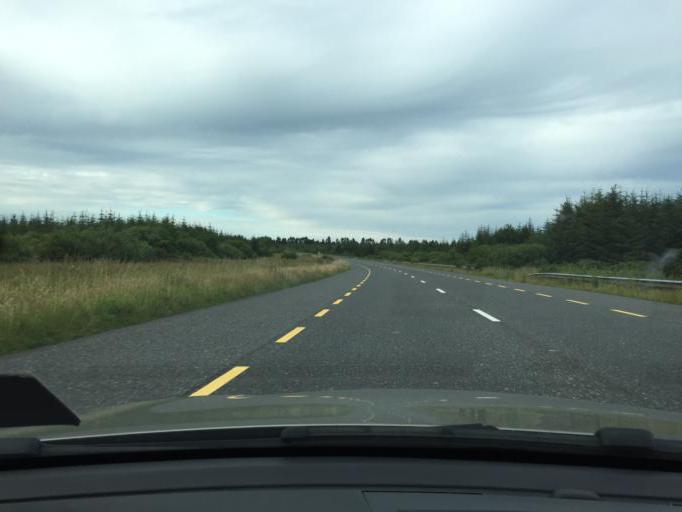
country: IE
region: Munster
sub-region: Waterford
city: Dungarvan
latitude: 52.0202
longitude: -7.6863
